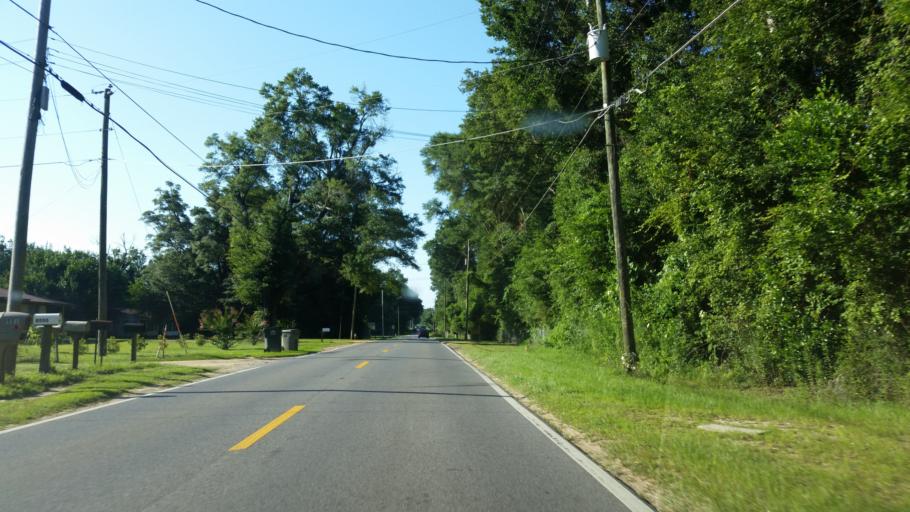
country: US
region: Florida
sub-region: Escambia County
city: Cantonment
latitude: 30.5265
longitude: -87.3808
